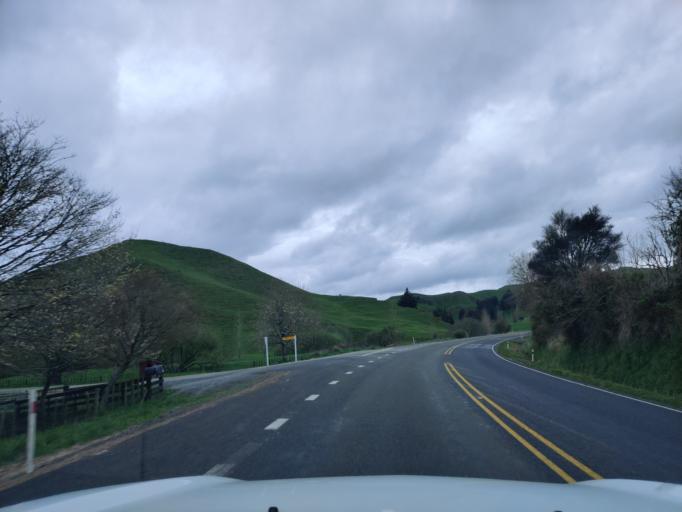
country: NZ
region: Waikato
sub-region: Otorohanga District
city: Otorohanga
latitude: -38.5242
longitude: 175.1754
